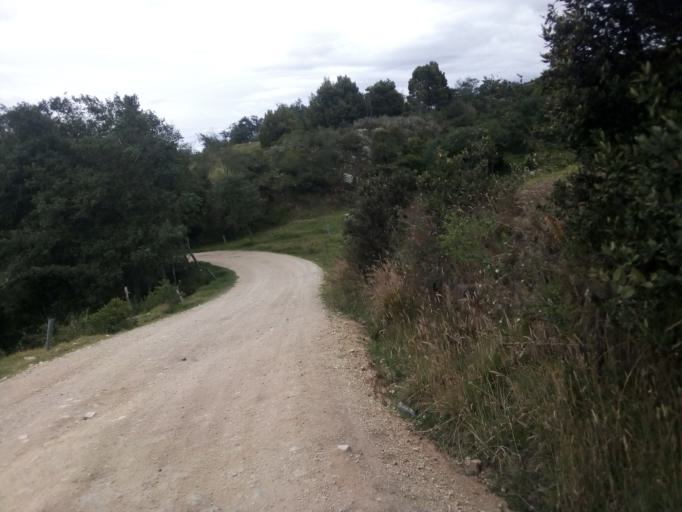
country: CO
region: Boyaca
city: Toca
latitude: 5.5809
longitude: -73.1444
